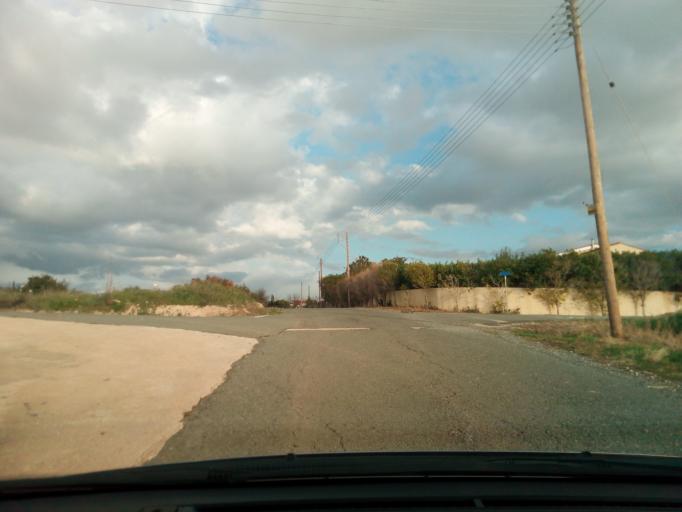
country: CY
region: Pafos
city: Pegeia
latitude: 34.8705
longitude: 32.3686
